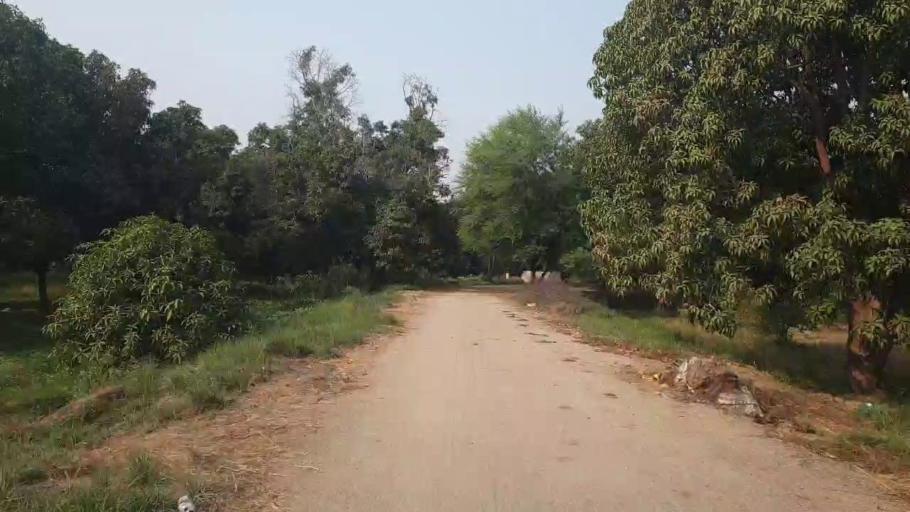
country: PK
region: Sindh
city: Tando Jam
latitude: 25.3336
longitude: 68.5150
